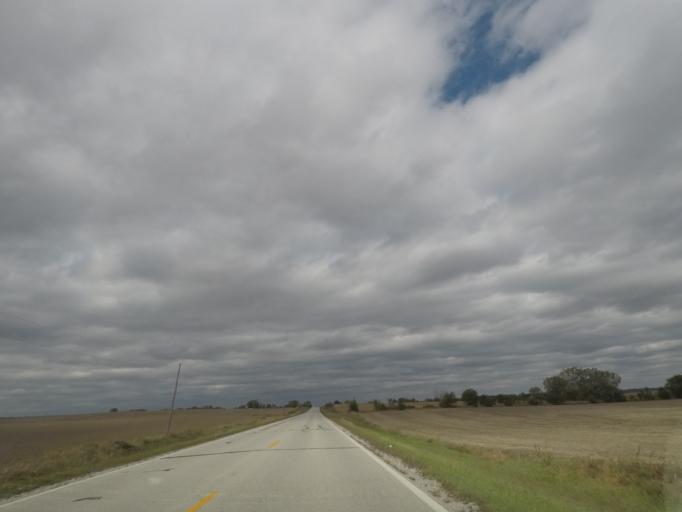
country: US
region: Iowa
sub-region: Story County
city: Huxley
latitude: 41.8549
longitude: -93.5316
